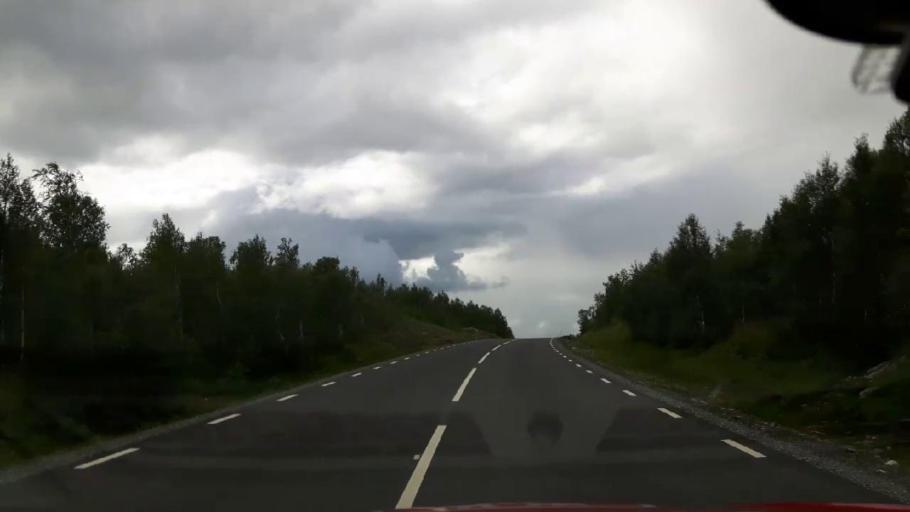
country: NO
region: Nord-Trondelag
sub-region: Royrvik
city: Royrvik
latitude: 64.9736
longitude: 14.2120
